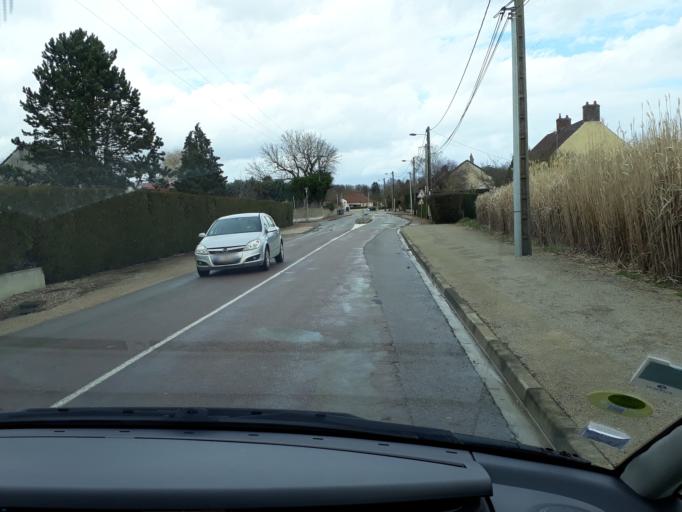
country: FR
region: Bourgogne
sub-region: Departement de la Cote-d'Or
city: Longecourt-en-Plaine
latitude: 47.2091
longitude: 5.1822
